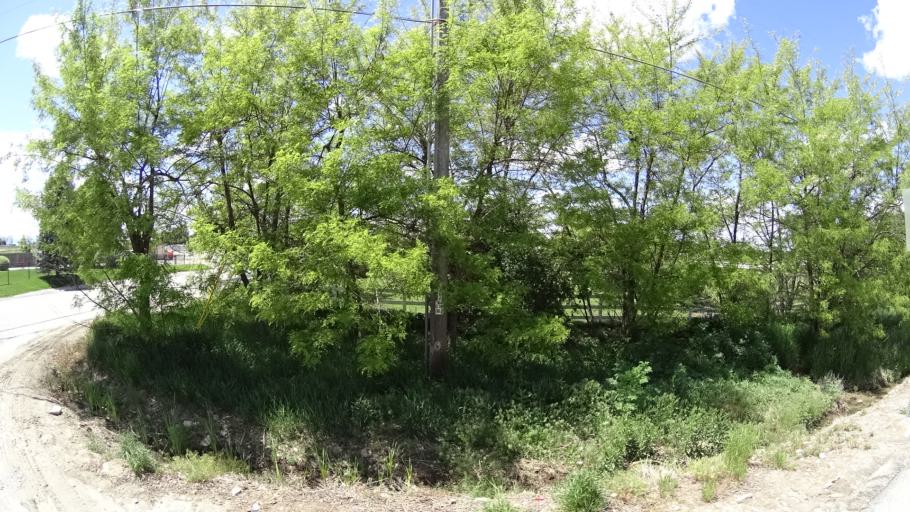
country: US
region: Idaho
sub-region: Ada County
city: Meridian
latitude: 43.5832
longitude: -116.4339
